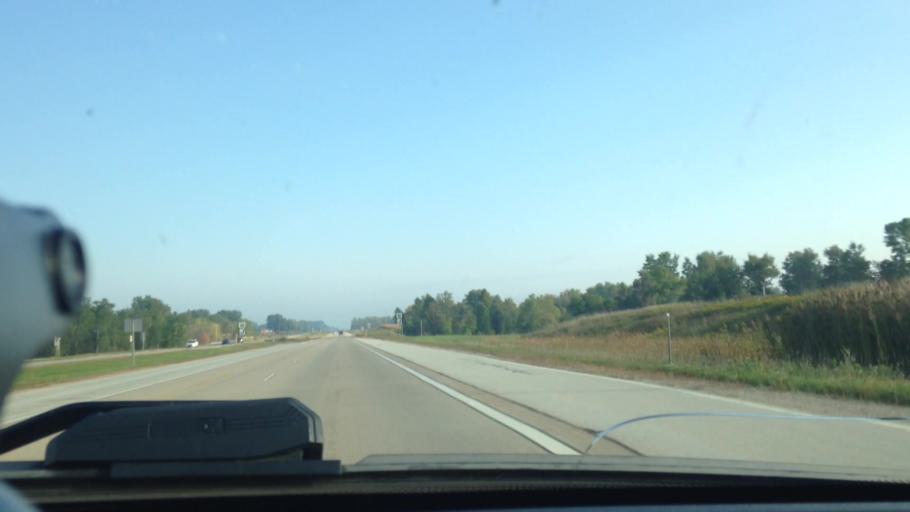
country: US
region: Wisconsin
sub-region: Oconto County
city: Oconto Falls
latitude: 45.0071
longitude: -88.0450
